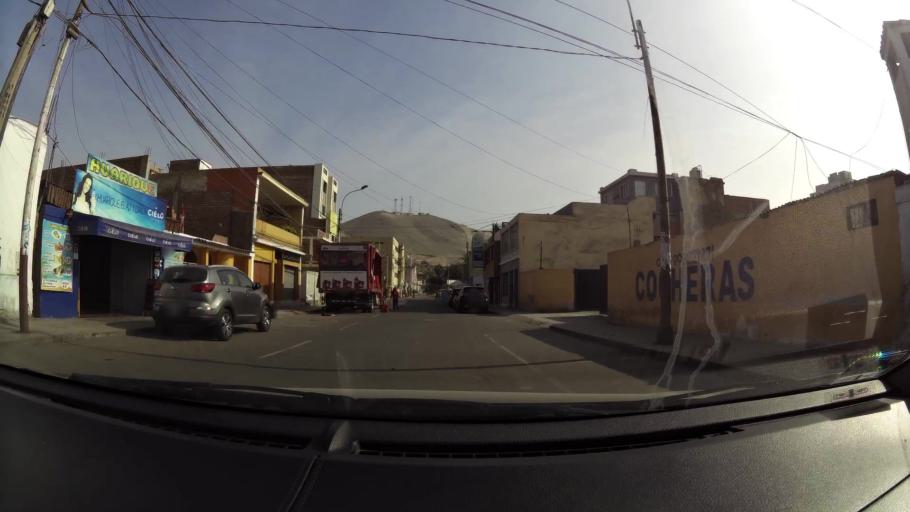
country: PE
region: Lima
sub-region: Lima
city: Santa Rosa
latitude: -11.7729
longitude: -77.1738
